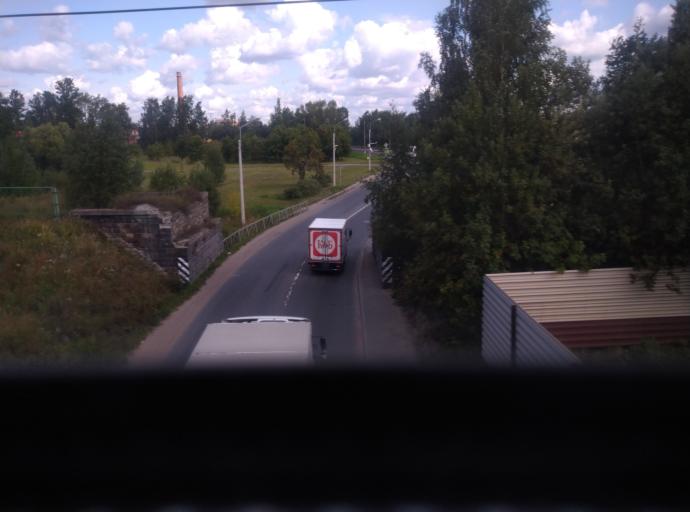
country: RU
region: St.-Petersburg
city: Kolpino
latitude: 59.7574
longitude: 30.5987
